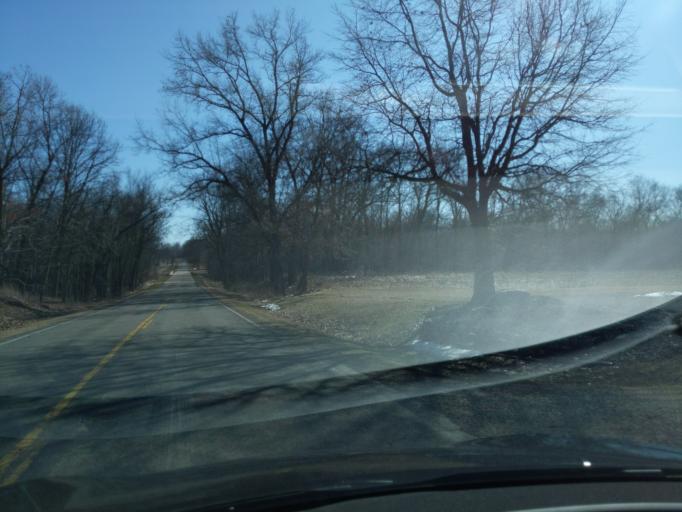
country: US
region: Michigan
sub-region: Ingham County
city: Leslie
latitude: 42.4060
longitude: -84.4434
